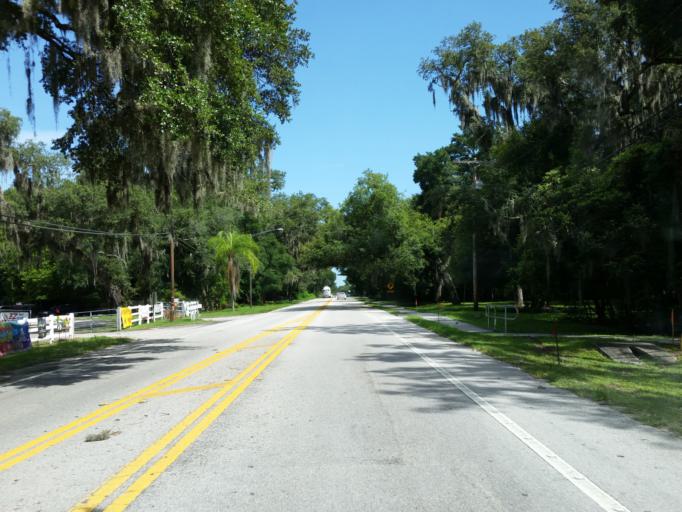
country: US
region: Florida
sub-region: Hillsborough County
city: Bloomingdale
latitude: 27.8976
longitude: -82.2473
